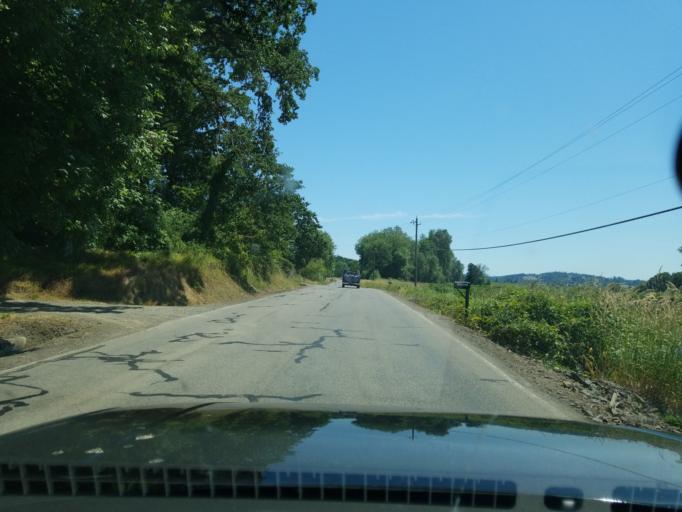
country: US
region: Oregon
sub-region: Yamhill County
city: Yamhill
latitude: 45.3396
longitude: -123.2175
